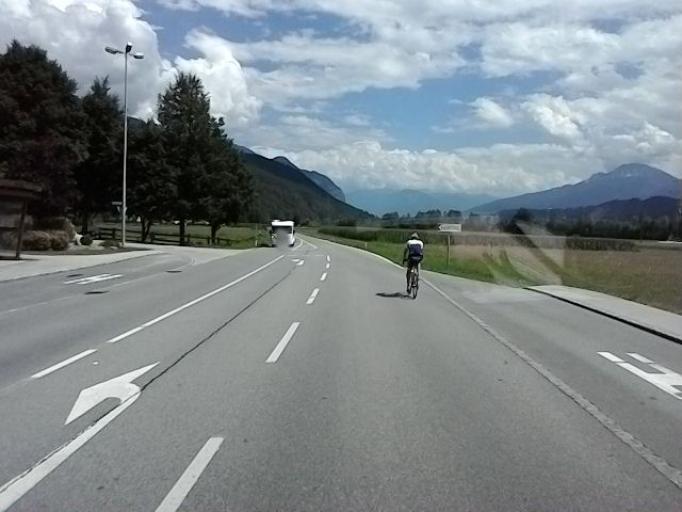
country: AT
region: Tyrol
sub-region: Politischer Bezirk Innsbruck Land
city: Hatting
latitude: 47.2886
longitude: 11.1699
